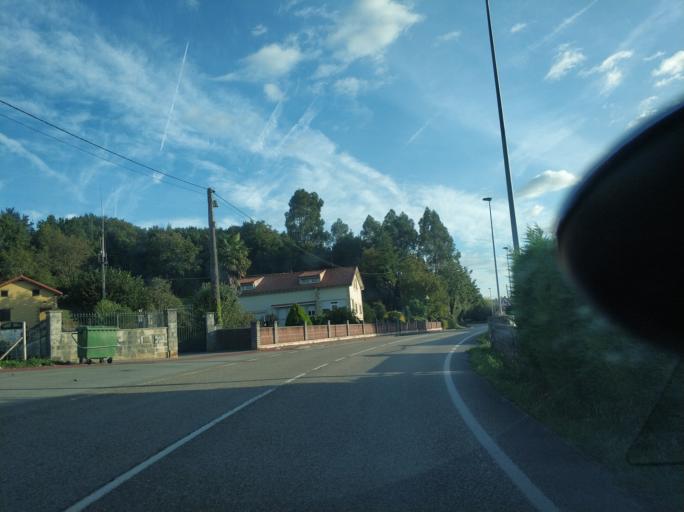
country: ES
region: Cantabria
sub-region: Provincia de Cantabria
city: Miengo
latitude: 43.4054
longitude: -3.9516
